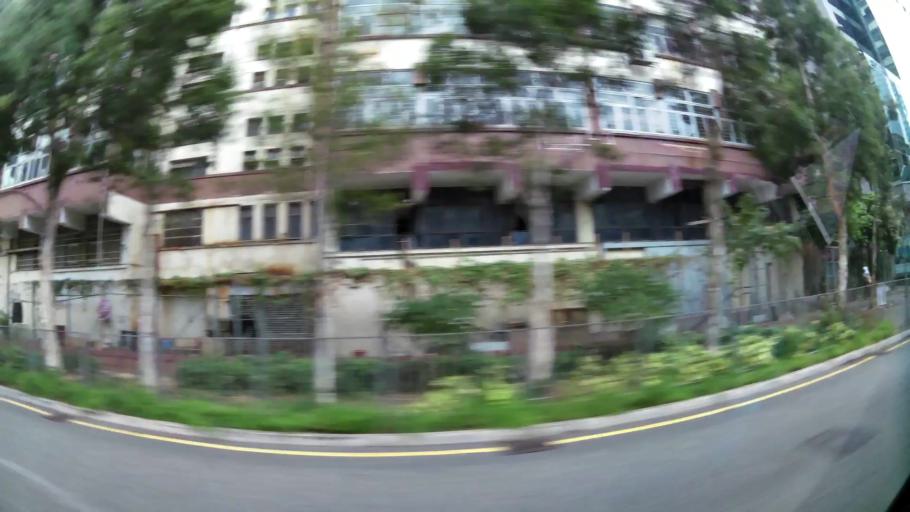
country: HK
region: Sham Shui Po
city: Sham Shui Po
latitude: 22.3205
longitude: 114.1599
